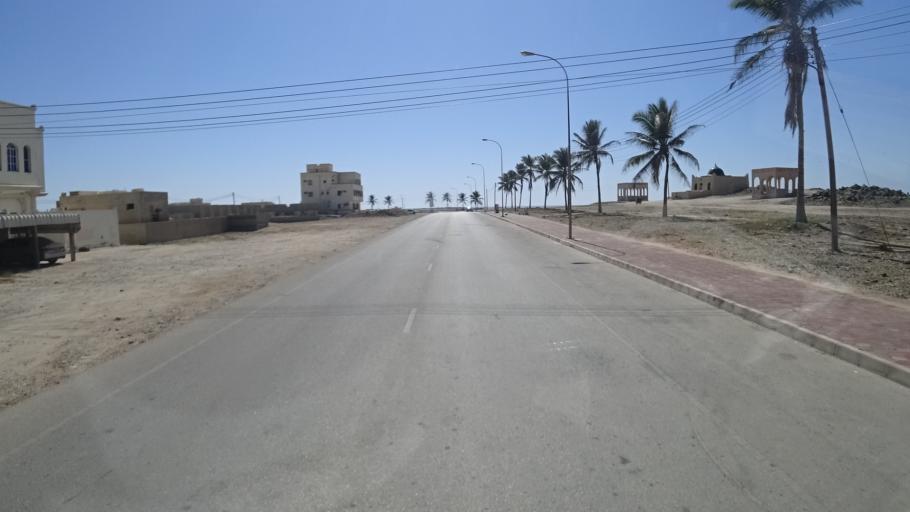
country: OM
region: Zufar
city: Salalah
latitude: 16.9788
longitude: 54.6875
